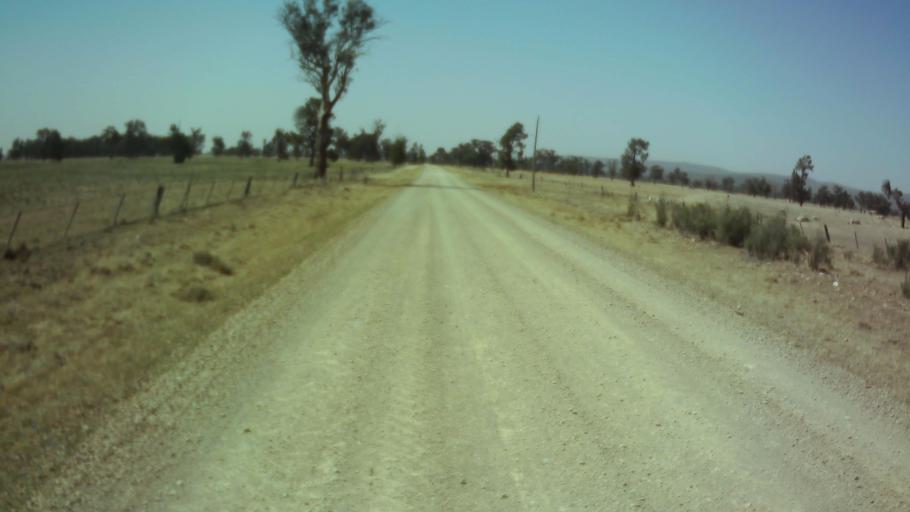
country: AU
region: New South Wales
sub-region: Weddin
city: Grenfell
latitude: -34.0267
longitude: 147.9134
